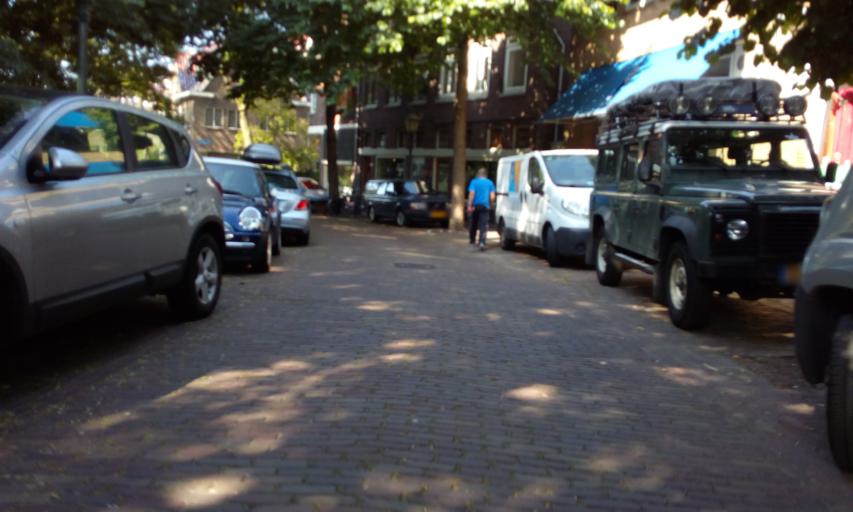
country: NL
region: South Holland
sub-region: Gemeente Lansingerland
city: Bergschenhoek
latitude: 51.9568
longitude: 4.4932
